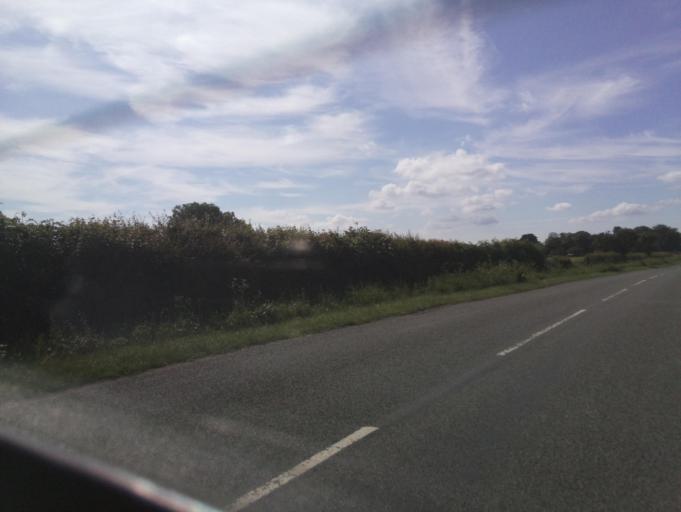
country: GB
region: England
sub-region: Lincolnshire
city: Skellingthorpe
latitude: 53.1423
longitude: -0.6331
